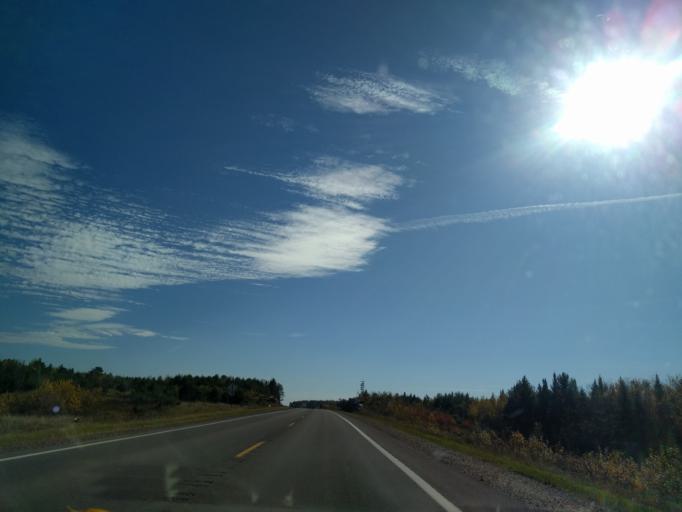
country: US
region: Michigan
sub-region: Marquette County
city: West Ishpeming
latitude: 46.3724
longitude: -87.9905
